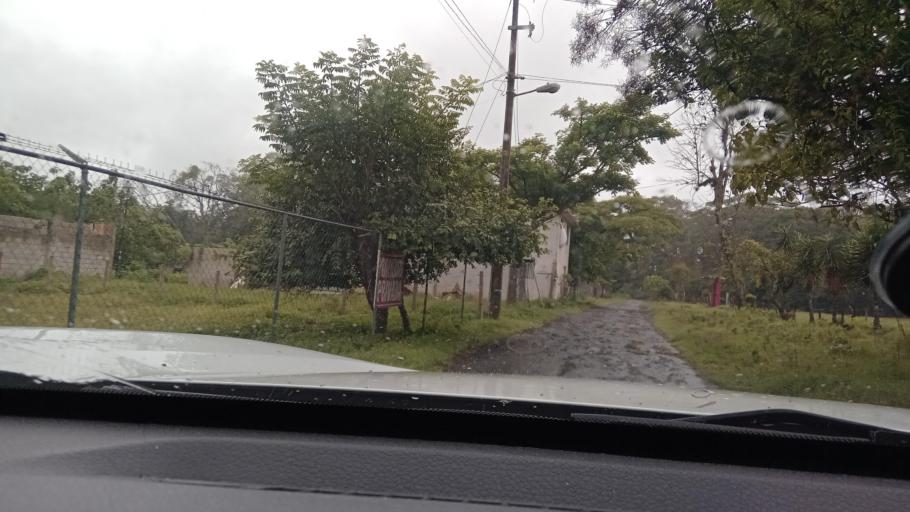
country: MX
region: Veracruz
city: Coatepec
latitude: 19.4567
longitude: -96.9782
